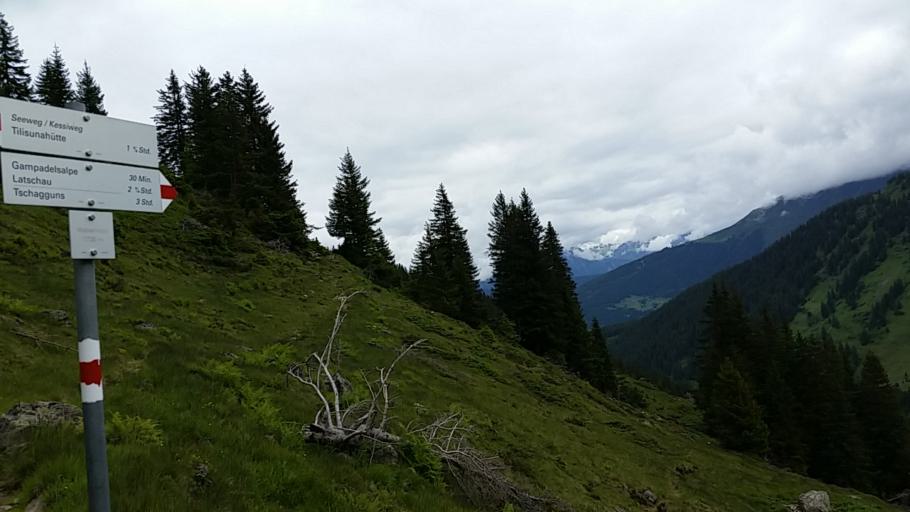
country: AT
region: Vorarlberg
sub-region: Politischer Bezirk Bludenz
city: Schruns
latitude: 47.0371
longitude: 9.8848
